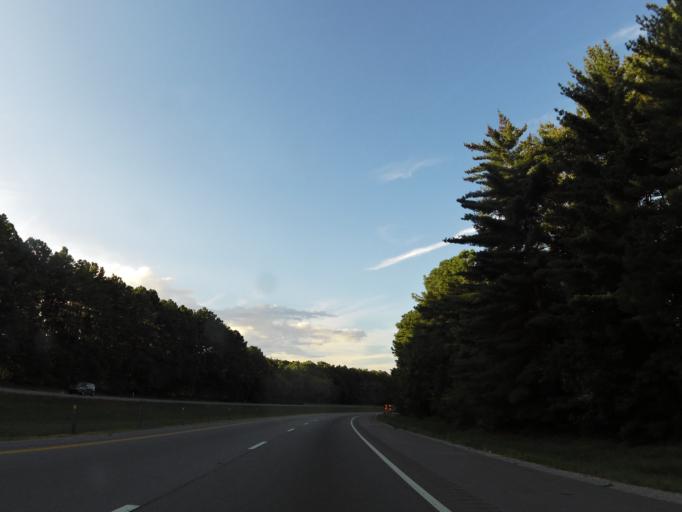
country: US
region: Tennessee
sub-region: Putnam County
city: Baxter
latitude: 36.1183
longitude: -85.6851
